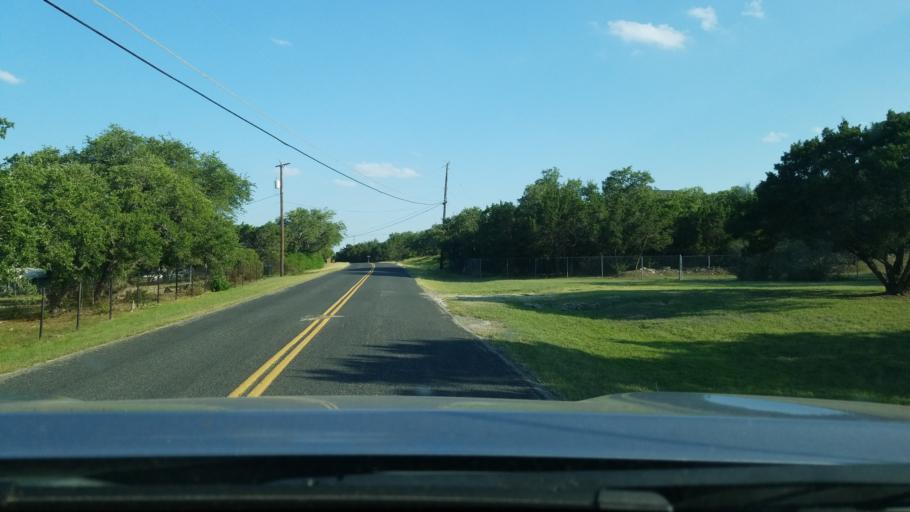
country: US
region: Texas
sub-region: Bexar County
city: Timberwood Park
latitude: 29.7026
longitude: -98.4376
